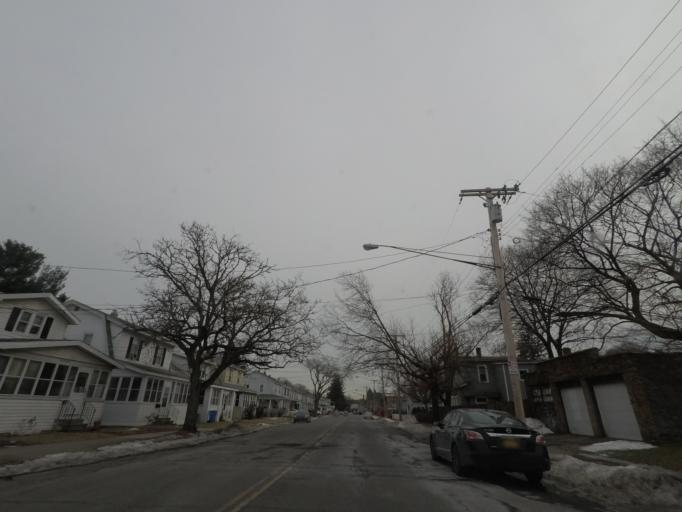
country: US
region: New York
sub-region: Albany County
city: West Albany
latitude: 42.6745
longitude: -73.7900
